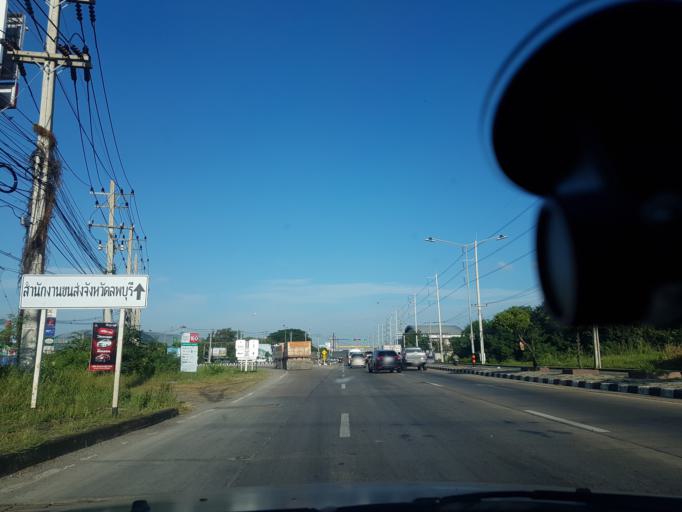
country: TH
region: Lop Buri
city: Lop Buri
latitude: 14.7748
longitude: 100.6967
